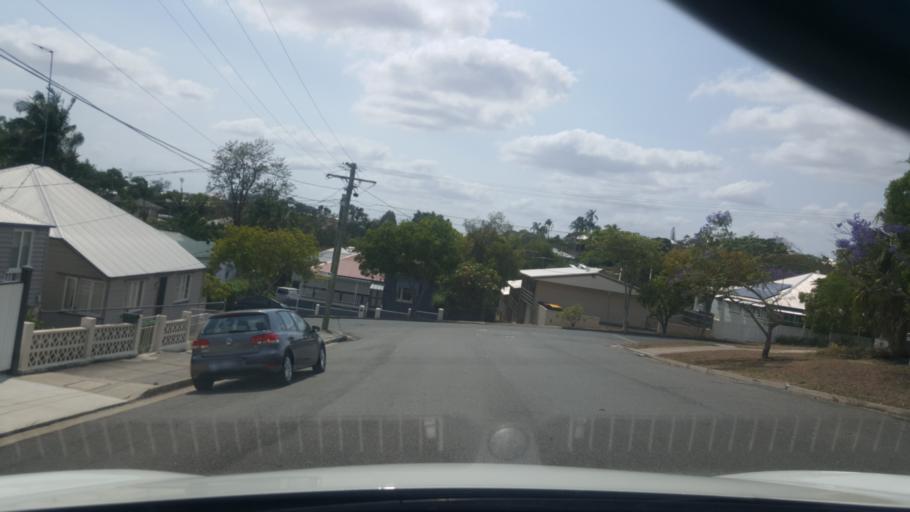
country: AU
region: Queensland
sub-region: Brisbane
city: South Brisbane
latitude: -27.4894
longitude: 153.0225
